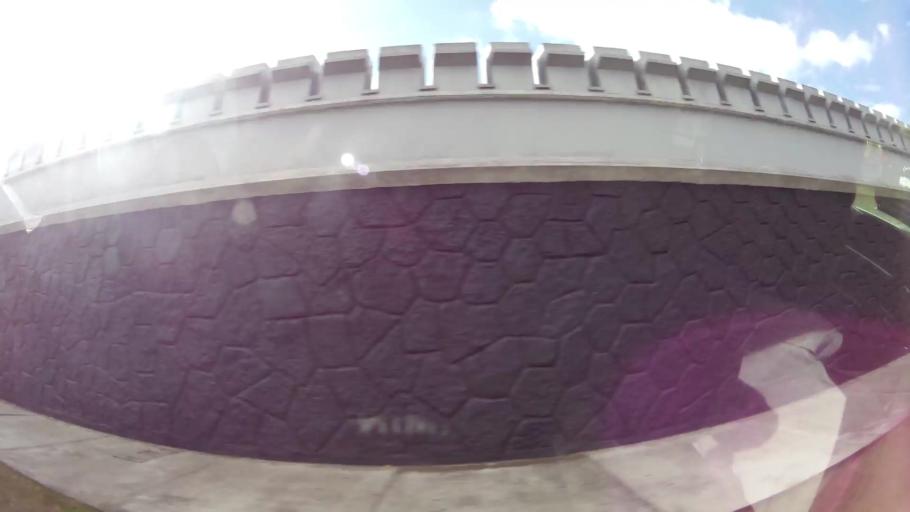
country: GT
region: Guatemala
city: Guatemala City
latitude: 14.6138
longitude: -90.5126
